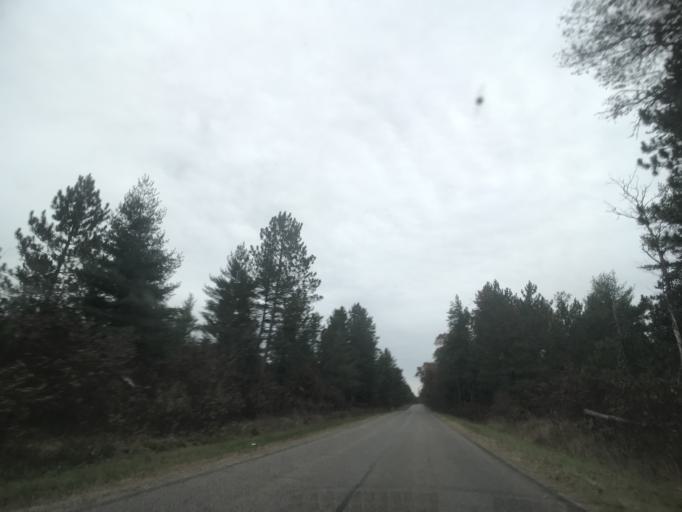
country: US
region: Wisconsin
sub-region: Oconto County
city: Gillett
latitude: 45.2574
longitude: -88.2521
